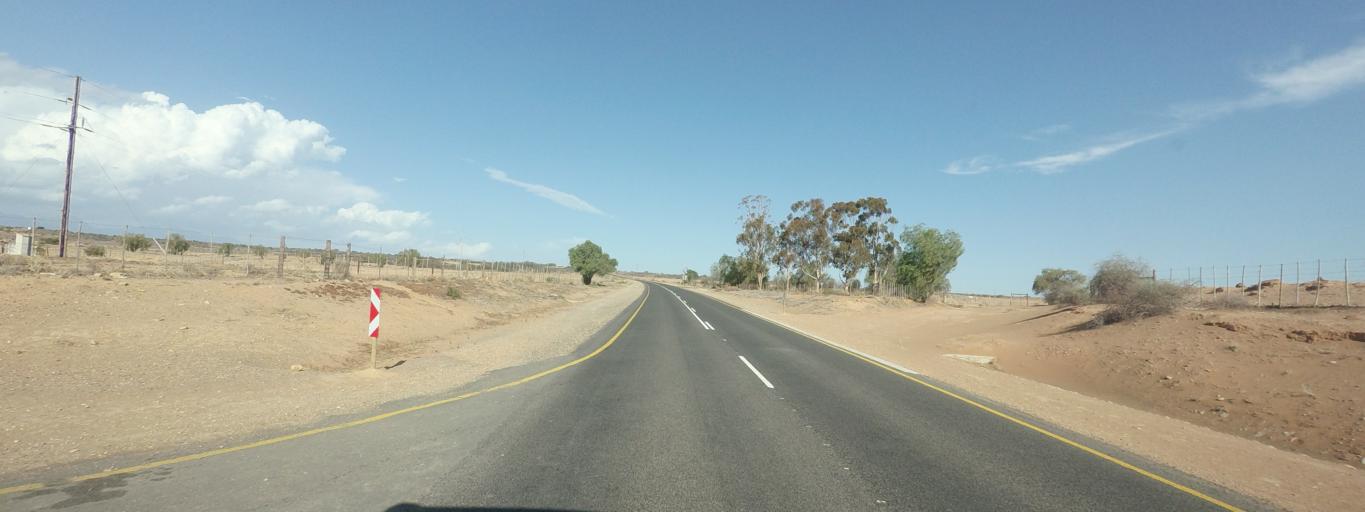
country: ZA
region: Western Cape
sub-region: Eden District Municipality
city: Oudtshoorn
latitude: -33.6035
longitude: 22.0635
